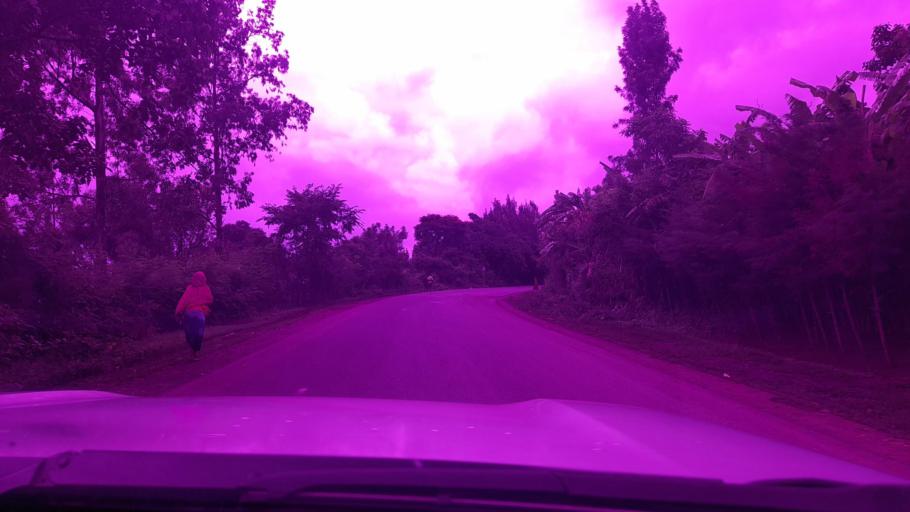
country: ET
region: Oromiya
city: Jima
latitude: 7.9208
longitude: 37.4088
